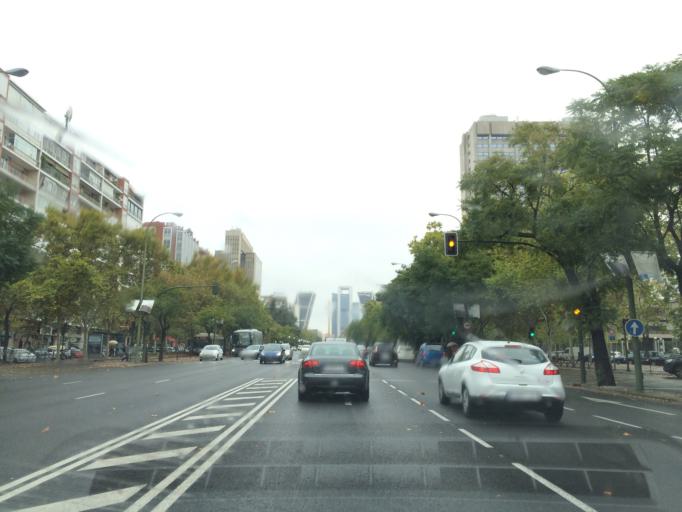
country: ES
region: Madrid
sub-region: Provincia de Madrid
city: Chamartin
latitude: 40.4561
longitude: -3.6903
